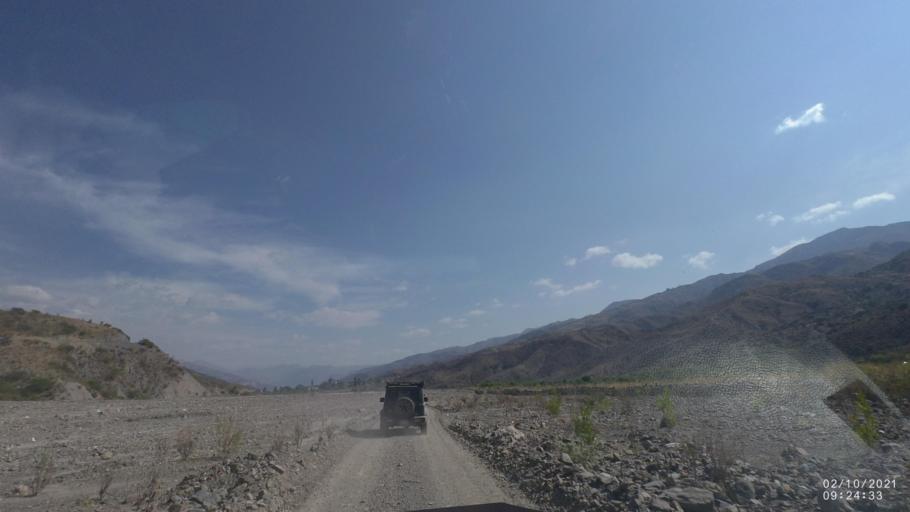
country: BO
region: Cochabamba
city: Irpa Irpa
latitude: -17.8637
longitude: -66.3125
